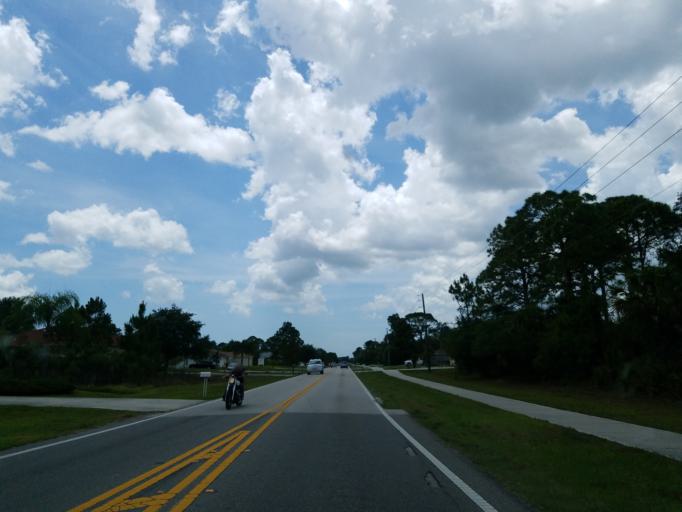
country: US
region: Florida
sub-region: Sarasota County
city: North Port
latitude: 27.0688
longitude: -82.1862
